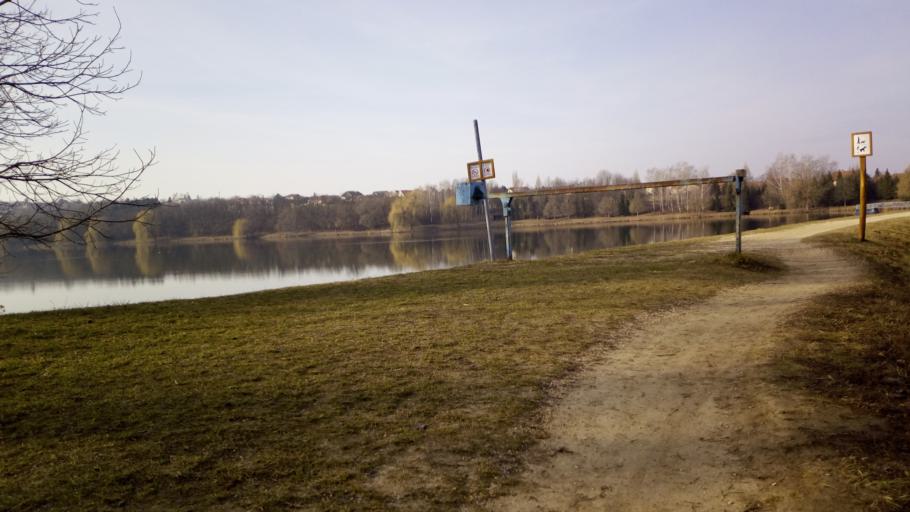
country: HU
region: Baranya
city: Pellerd
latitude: 46.0204
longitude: 18.2011
